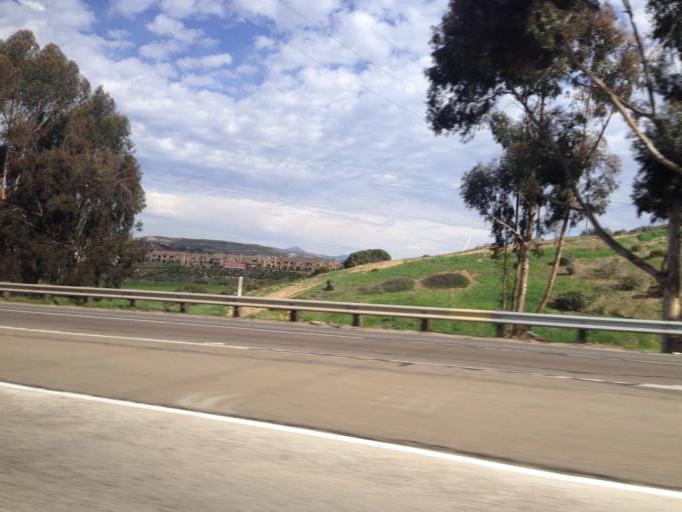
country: US
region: California
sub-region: San Diego County
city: Bonita
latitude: 32.5876
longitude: -117.0362
